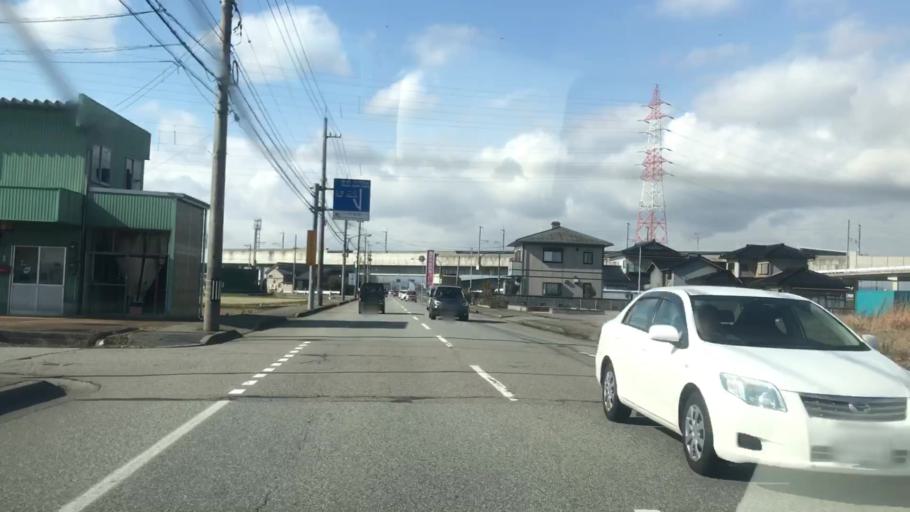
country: JP
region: Toyama
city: Nishishinminato
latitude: 36.7216
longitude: 137.0732
